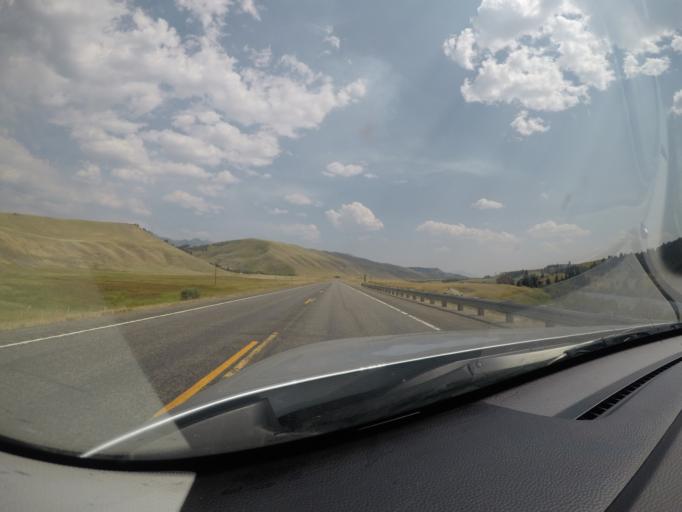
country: US
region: Montana
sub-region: Gallatin County
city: Big Sky
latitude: 44.9649
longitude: -111.6348
